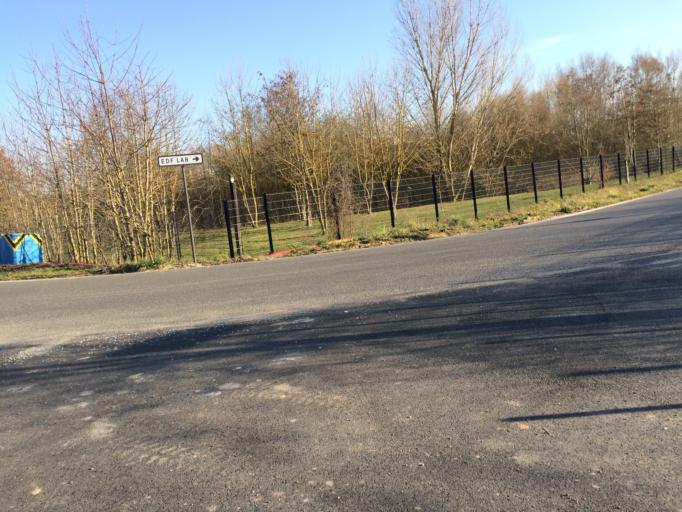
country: FR
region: Ile-de-France
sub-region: Departement de l'Essonne
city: Vauhallan
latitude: 48.7186
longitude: 2.1990
